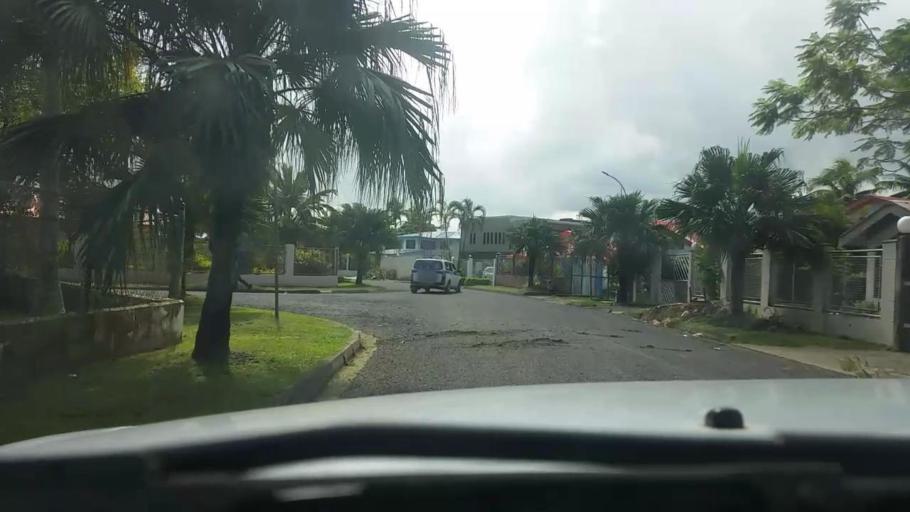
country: FJ
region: Central
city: Suva
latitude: -18.1316
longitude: 178.4662
